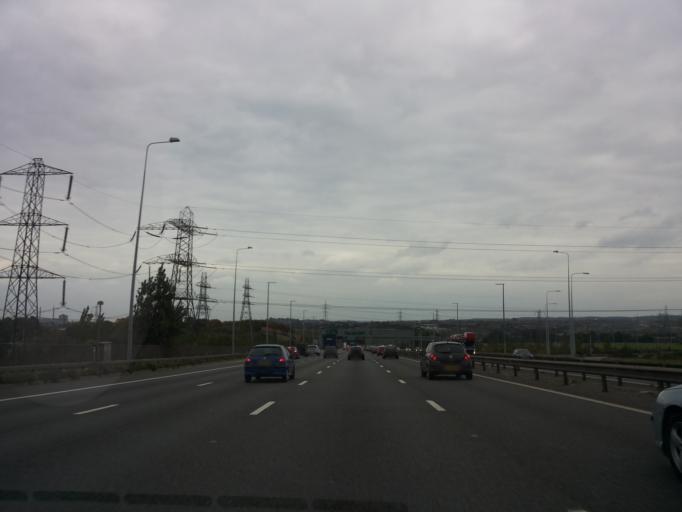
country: GB
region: England
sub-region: Kent
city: Swanscombe
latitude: 51.4305
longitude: 0.3094
